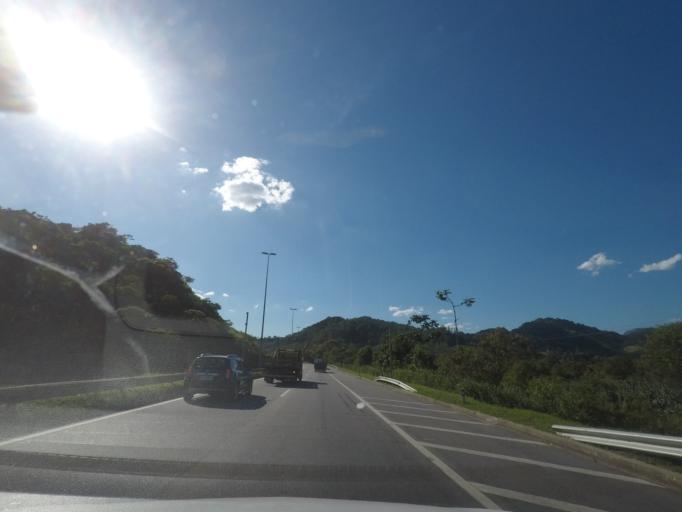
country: BR
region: Rio de Janeiro
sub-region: Petropolis
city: Petropolis
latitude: -22.6569
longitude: -43.1200
